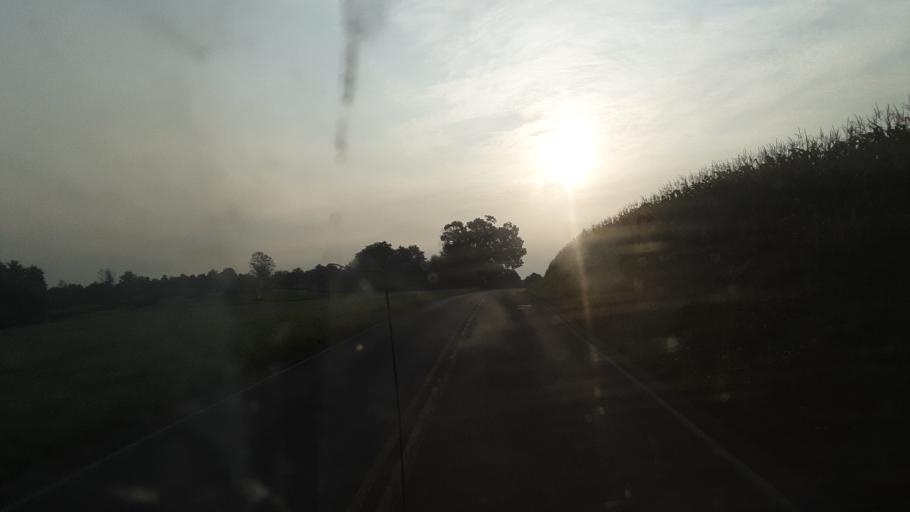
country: US
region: Pennsylvania
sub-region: Clarion County
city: Clarion
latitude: 40.9886
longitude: -79.2916
